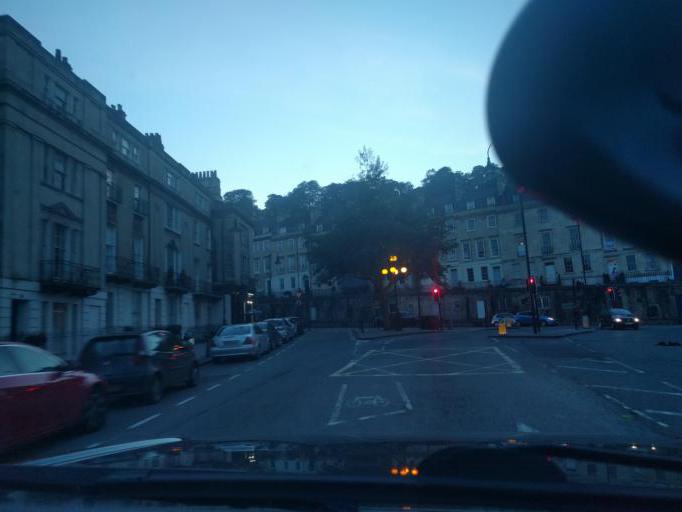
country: GB
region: England
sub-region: Bath and North East Somerset
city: Bath
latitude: 51.3898
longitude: -2.3564
